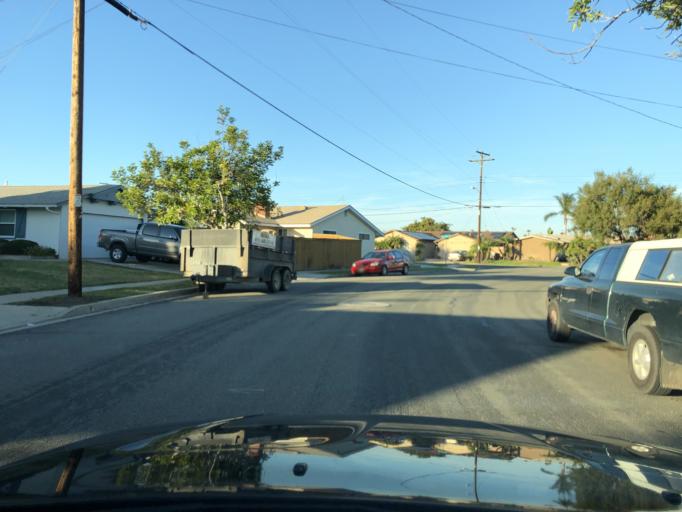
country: US
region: California
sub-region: San Diego County
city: La Jolla
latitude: 32.8206
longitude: -117.1940
